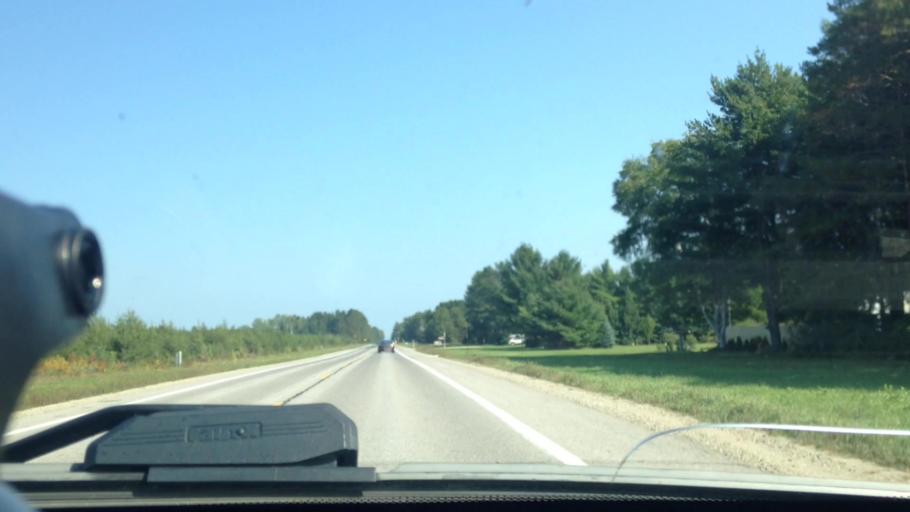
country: US
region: Michigan
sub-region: Luce County
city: Newberry
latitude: 46.3036
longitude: -85.4552
